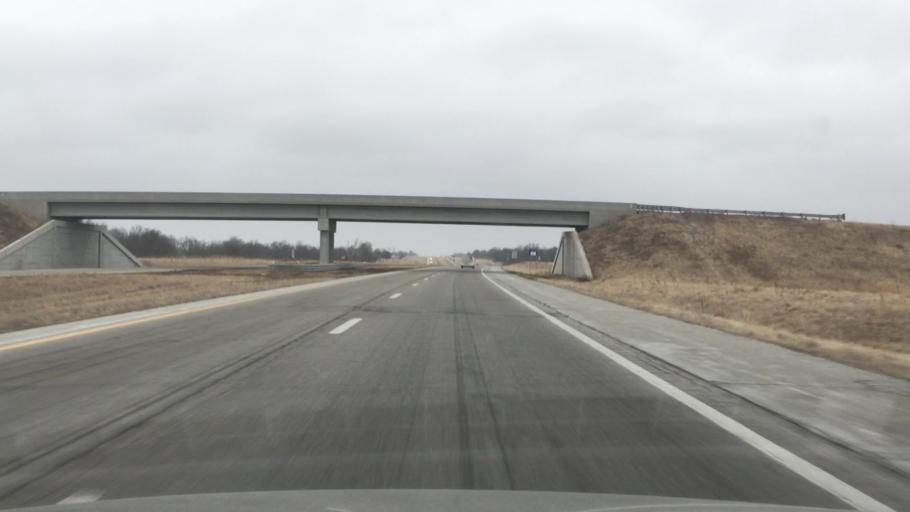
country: US
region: Missouri
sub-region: Cass County
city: Harrisonville
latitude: 38.6039
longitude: -94.3492
